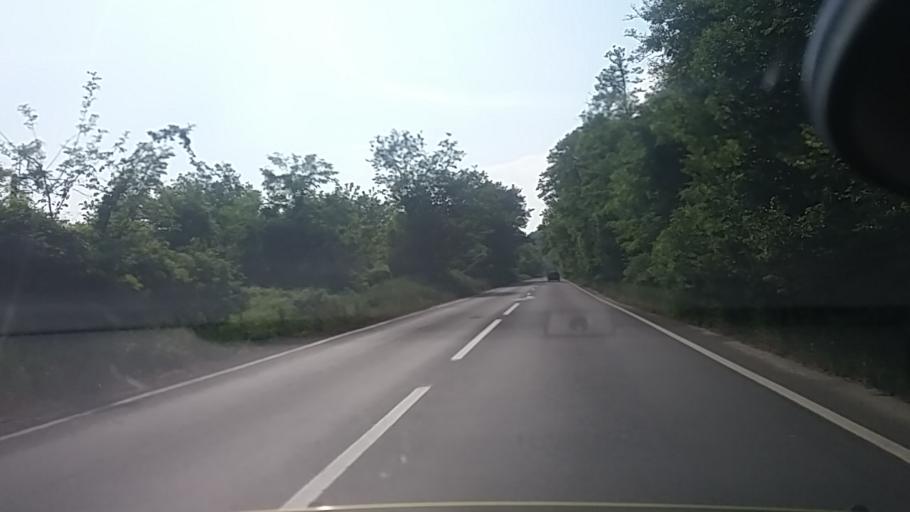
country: RO
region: Arad
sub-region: Comuna Conop
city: Conop
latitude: 46.0975
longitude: 21.9106
